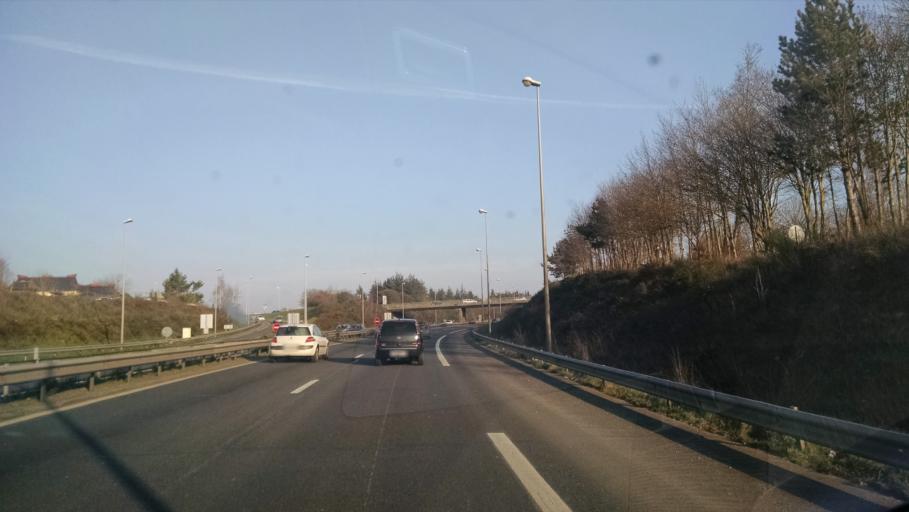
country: FR
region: Pays de la Loire
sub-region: Departement de la Loire-Atlantique
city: Saint-Herblain
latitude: 47.2089
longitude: -1.6267
